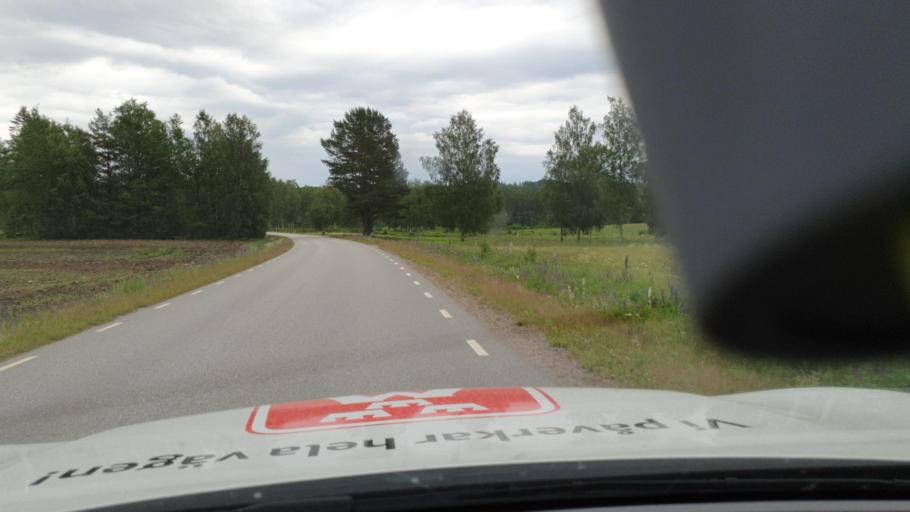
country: SE
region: Vaestra Goetaland
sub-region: Karlsborgs Kommun
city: Karlsborg
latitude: 58.6680
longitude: 14.4690
